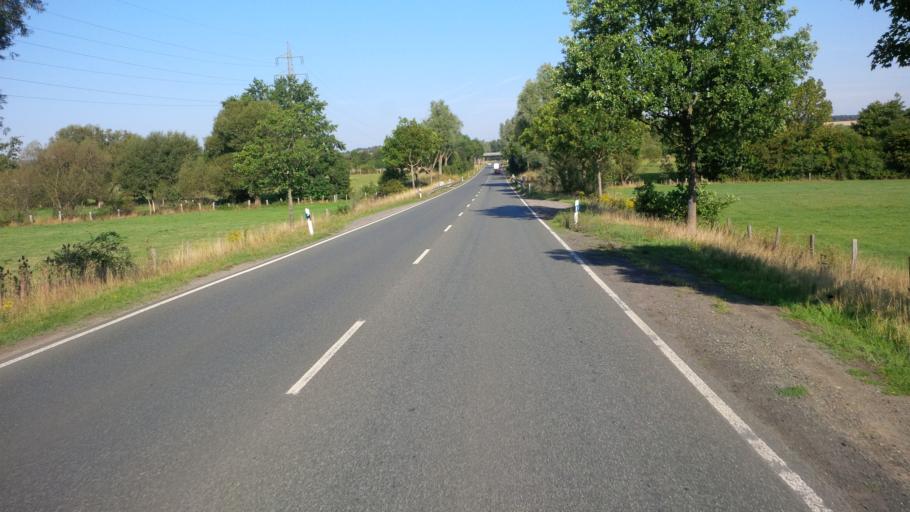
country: DE
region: Hesse
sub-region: Regierungsbezirk Darmstadt
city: Wehrheim
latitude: 50.2872
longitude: 8.5606
